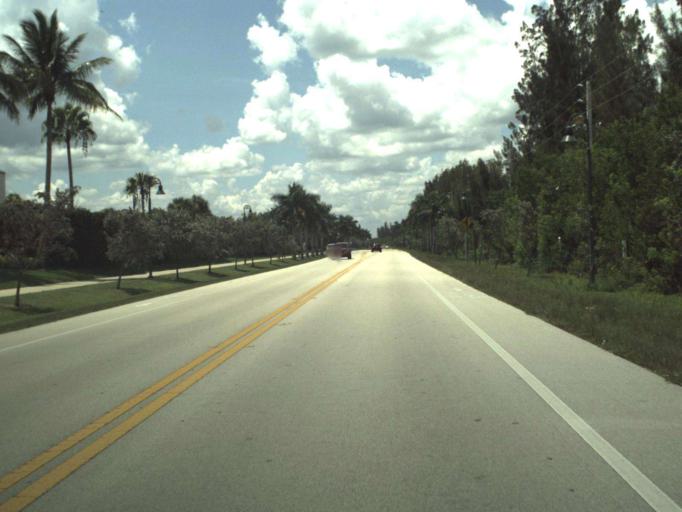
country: US
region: Florida
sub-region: Saint Lucie County
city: Fort Pierce
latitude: 27.4435
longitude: -80.2856
